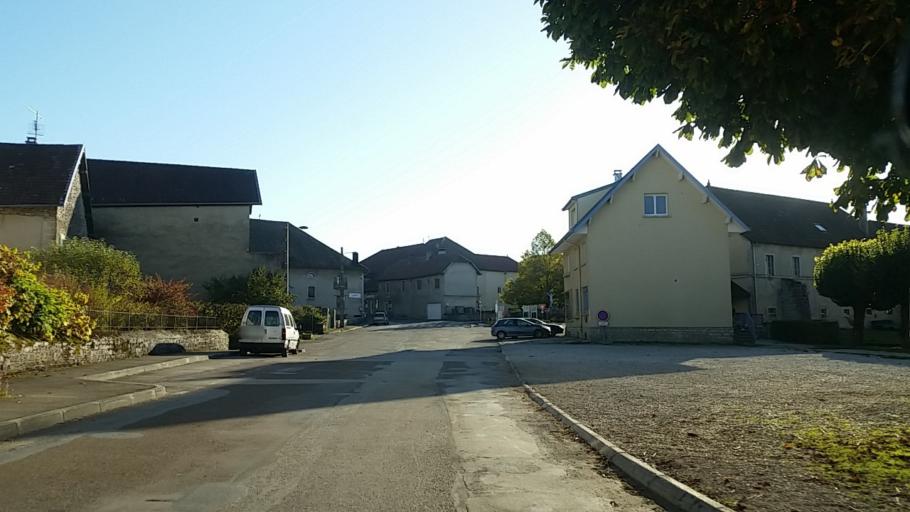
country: FR
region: Franche-Comte
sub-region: Departement du Doubs
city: Levier
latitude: 47.0389
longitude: 6.0719
